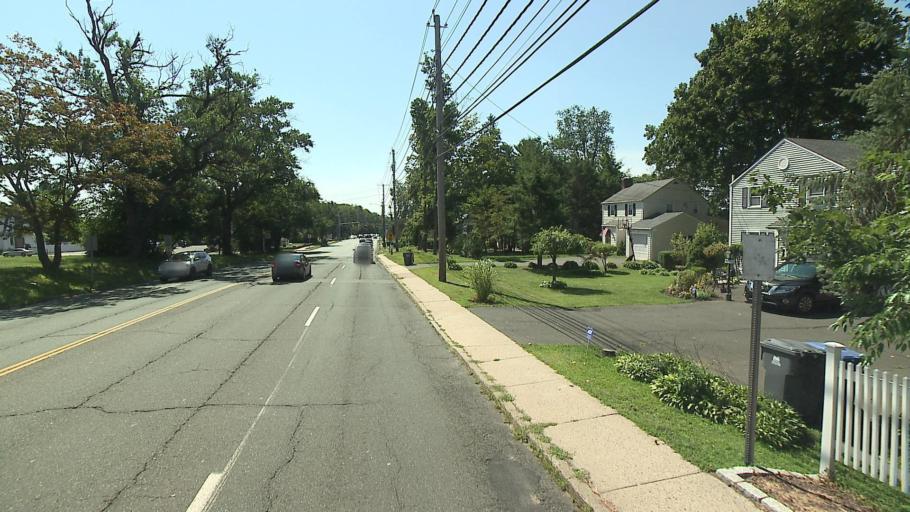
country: US
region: Connecticut
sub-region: Fairfield County
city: Trumbull
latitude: 41.2281
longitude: -73.2193
